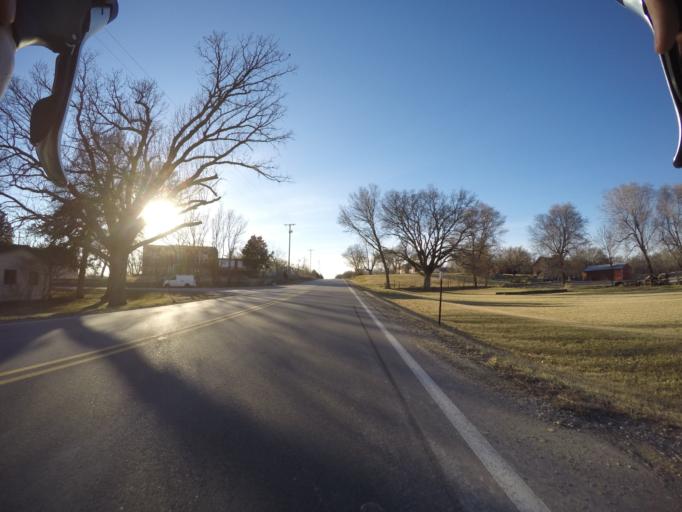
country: US
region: Kansas
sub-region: Riley County
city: Ogden
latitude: 39.2248
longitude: -96.7083
